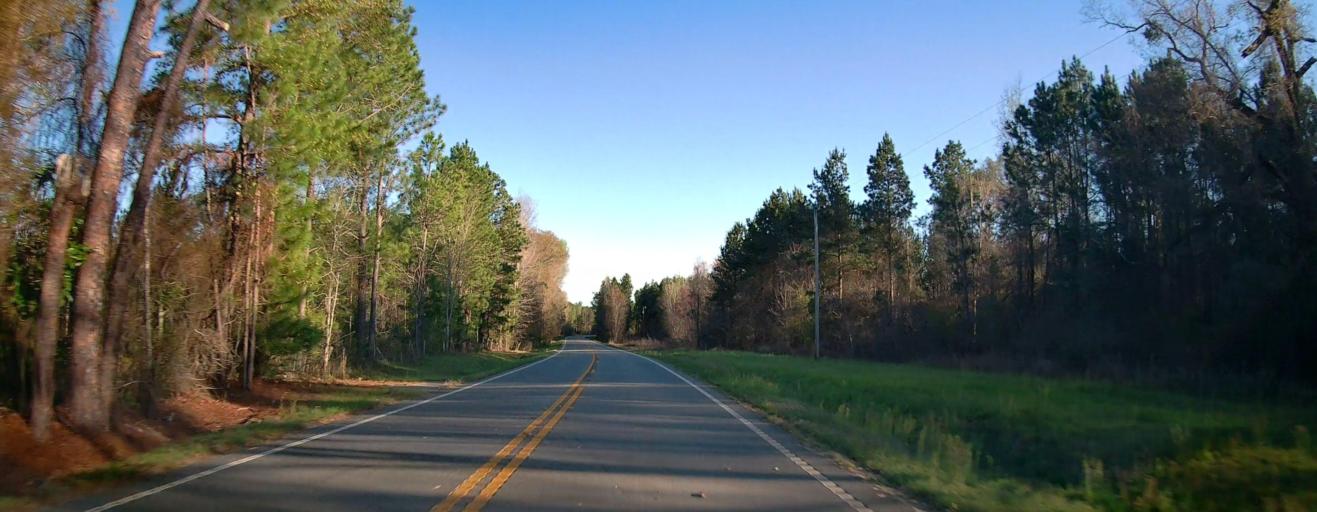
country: US
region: Georgia
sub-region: Pulaski County
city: Hawkinsville
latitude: 32.2001
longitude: -83.3737
